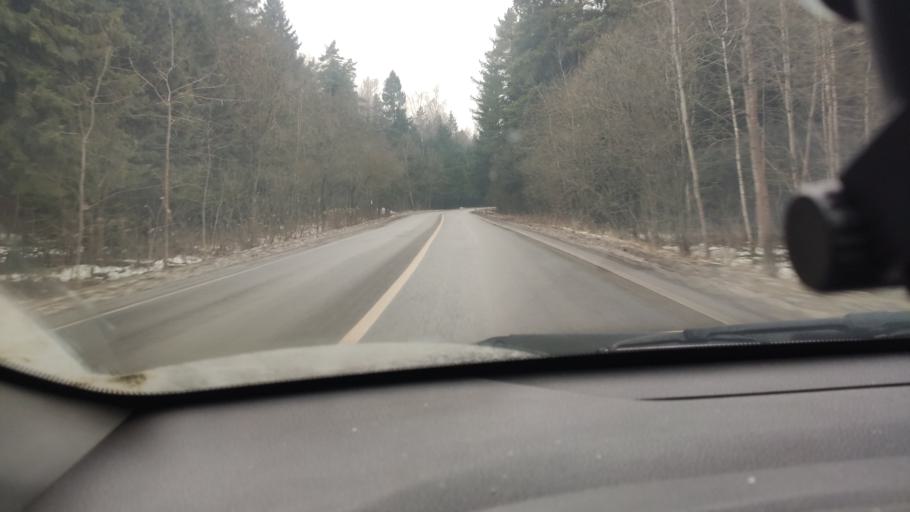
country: RU
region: Moskovskaya
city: Yakovlevskoye
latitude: 55.4556
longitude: 37.8821
